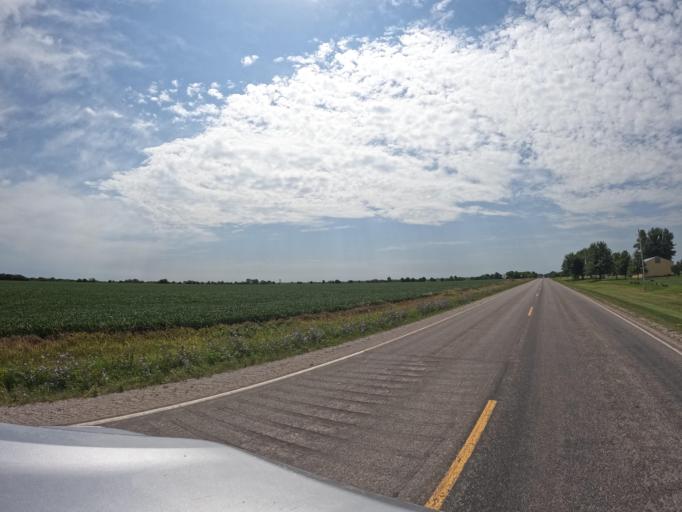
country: US
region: Iowa
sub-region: Appanoose County
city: Centerville
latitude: 40.8103
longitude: -92.9448
